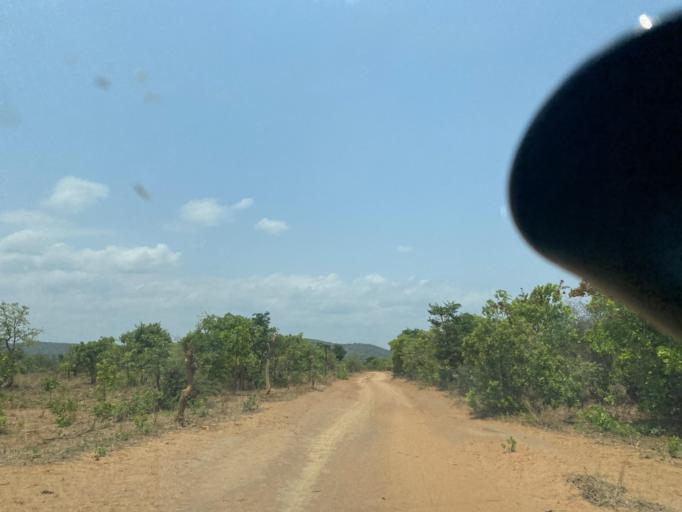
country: ZM
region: Lusaka
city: Chongwe
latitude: -15.5168
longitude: 28.8820
